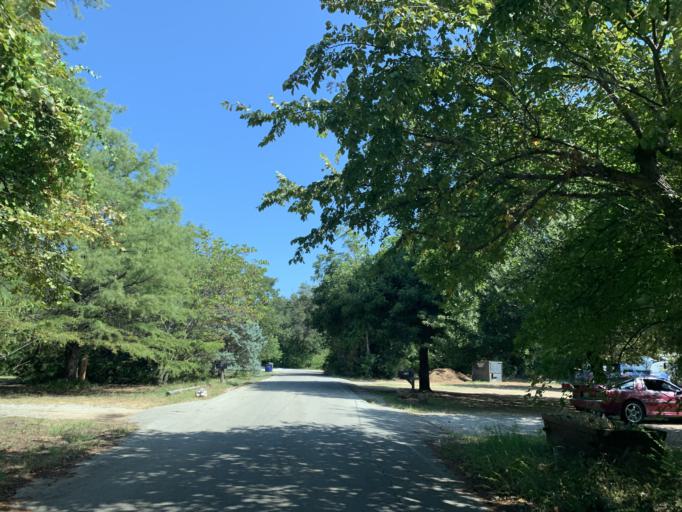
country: US
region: Texas
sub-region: Tarrant County
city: Azle
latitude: 32.8809
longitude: -97.5382
